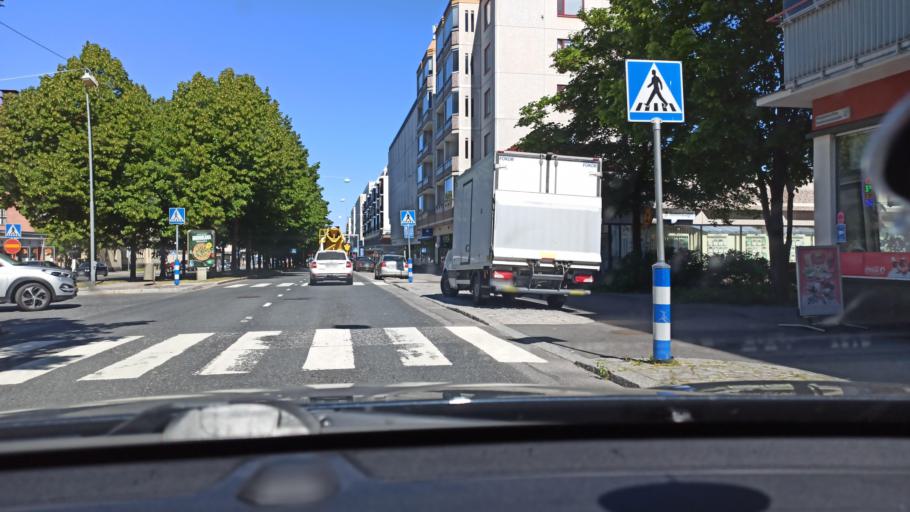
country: FI
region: Ostrobothnia
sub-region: Vaasa
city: Vaasa
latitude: 63.0921
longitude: 21.6194
